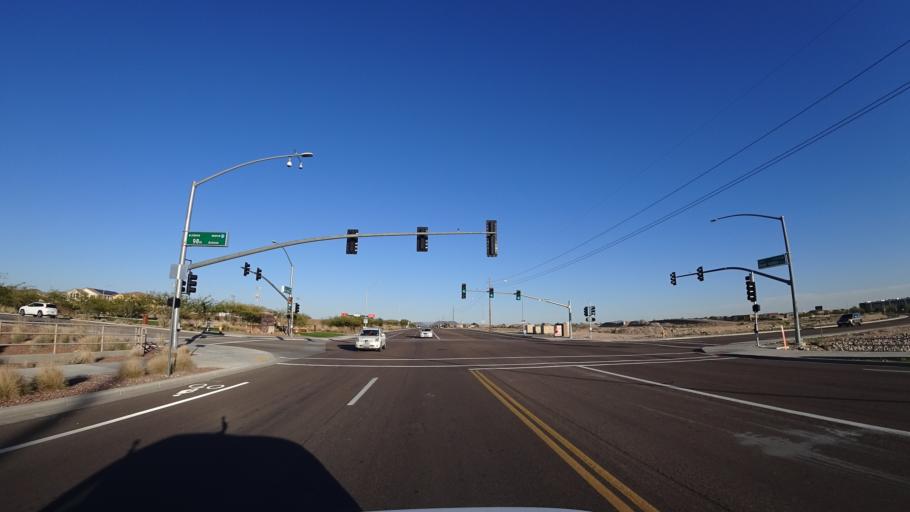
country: US
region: Arizona
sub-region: Maricopa County
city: Sun City West
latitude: 33.6818
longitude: -112.2704
